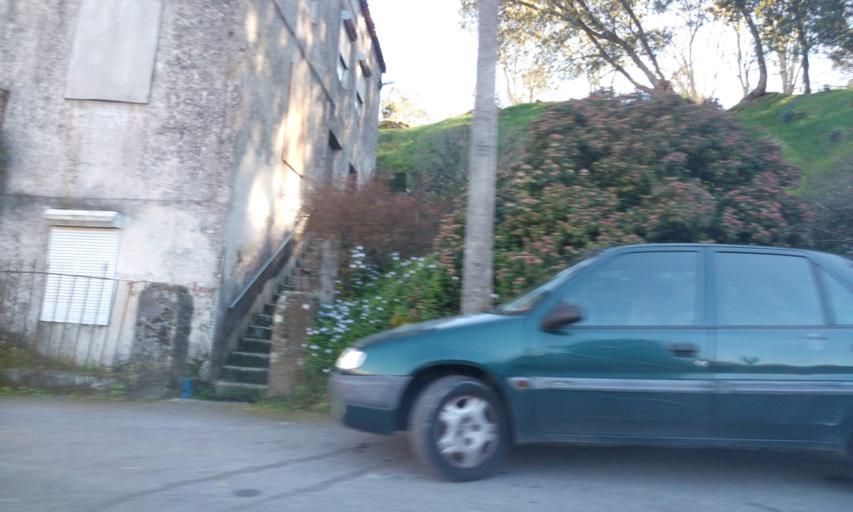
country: PT
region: Guarda
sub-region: Manteigas
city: Manteigas
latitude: 40.4904
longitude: -7.5918
